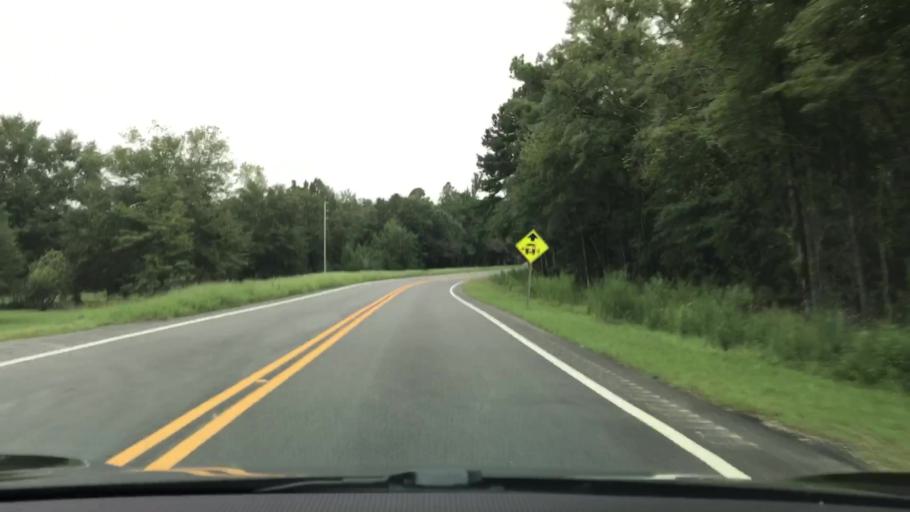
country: US
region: Alabama
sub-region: Covington County
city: Opp
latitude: 31.2266
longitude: -86.1615
